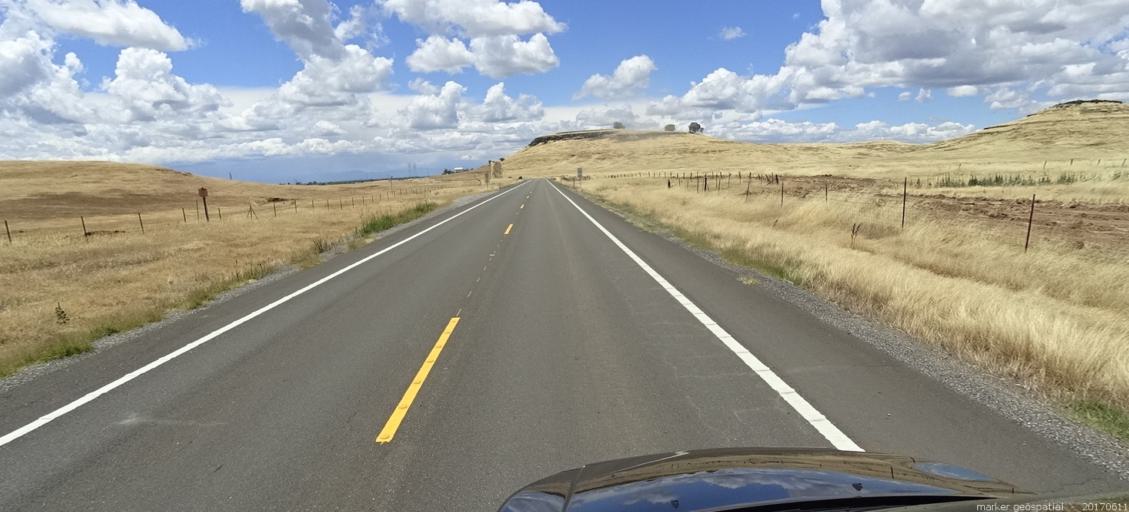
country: US
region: California
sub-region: Butte County
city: Durham
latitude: 39.6396
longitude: -121.6735
